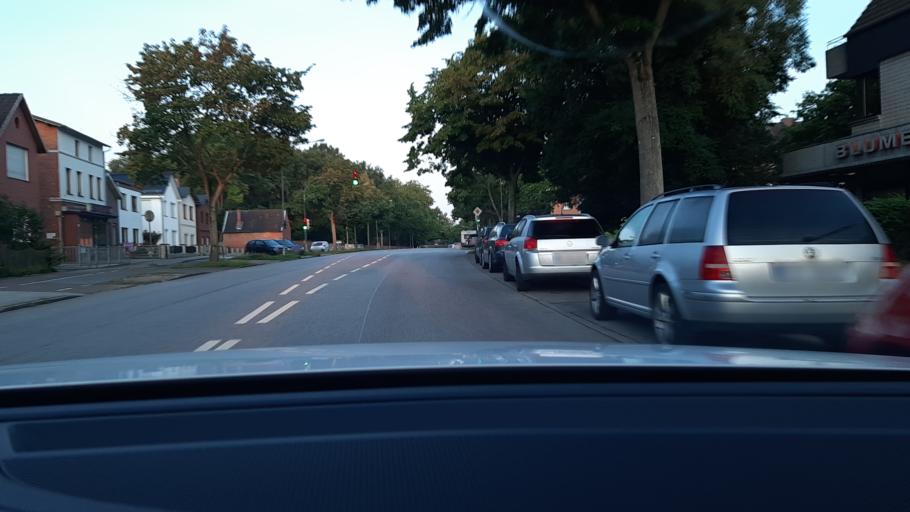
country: DE
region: Schleswig-Holstein
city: Stockelsdorf
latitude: 53.8418
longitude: 10.6377
